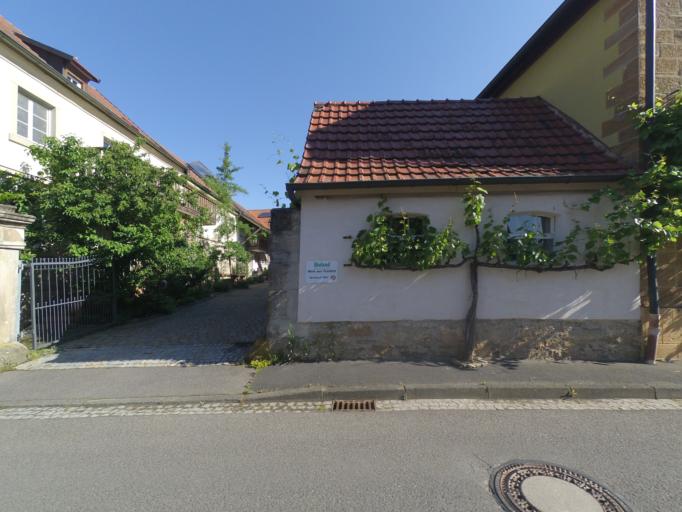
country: DE
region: Bavaria
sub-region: Regierungsbezirk Unterfranken
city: Gerolzhofen
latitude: 49.9090
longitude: 10.3582
